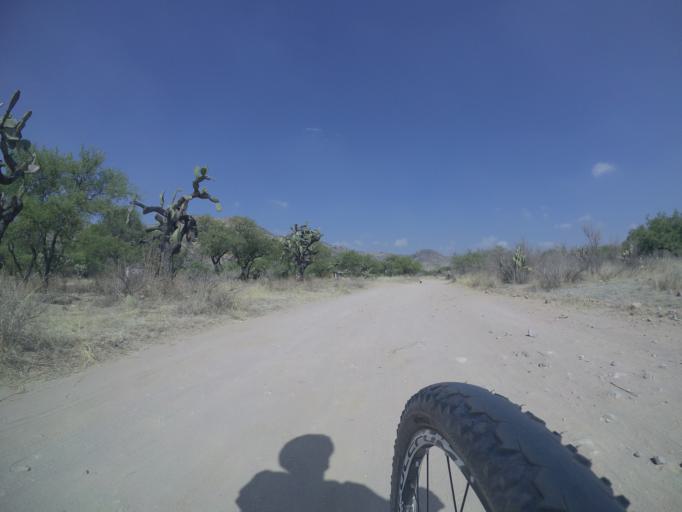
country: MX
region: Aguascalientes
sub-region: Jesus Maria
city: Paseos de las Haciendas [Fraccionamiento]
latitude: 22.0013
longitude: -102.3663
